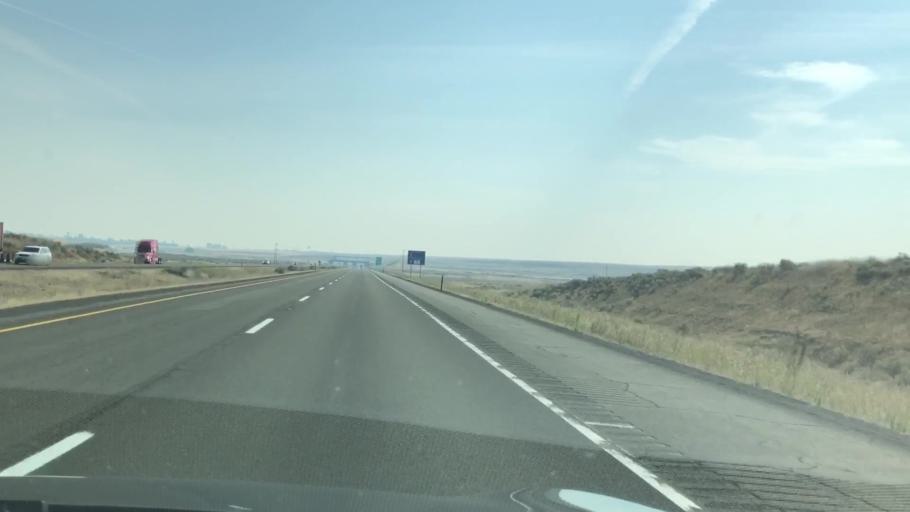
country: US
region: Washington
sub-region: Adams County
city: Ritzville
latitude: 47.1104
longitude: -118.4169
